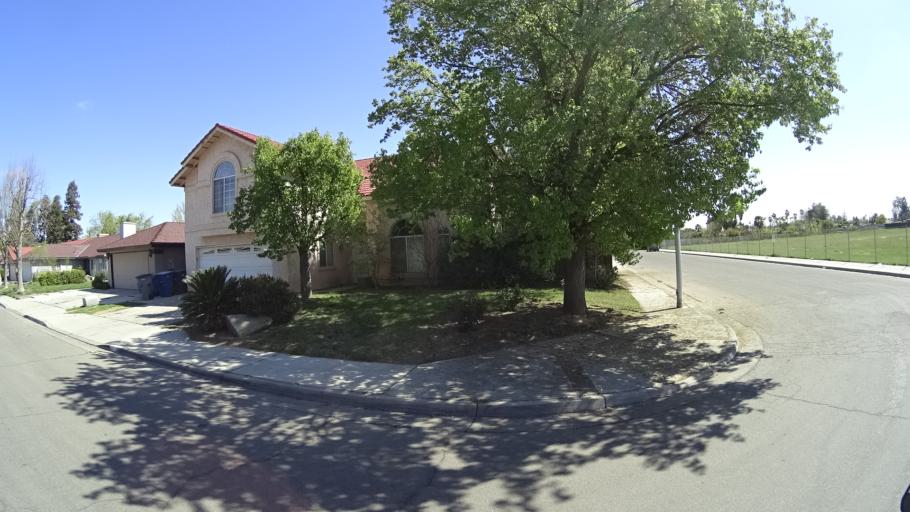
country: US
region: California
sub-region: Fresno County
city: West Park
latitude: 36.7828
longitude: -119.8847
